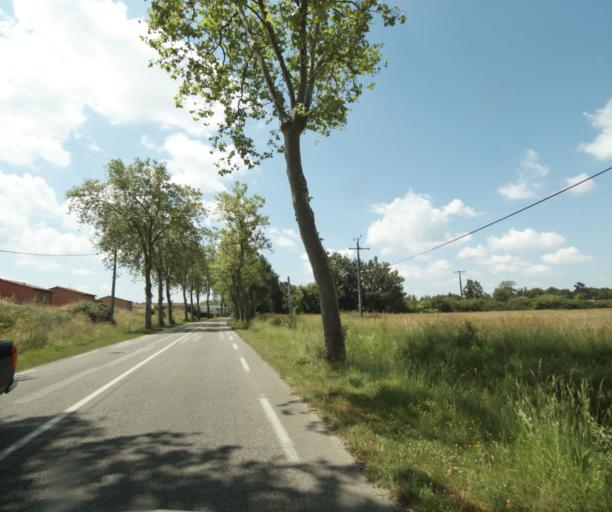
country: FR
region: Midi-Pyrenees
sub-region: Departement du Tarn-et-Garonne
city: Montauban
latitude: 44.0486
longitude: 1.3582
